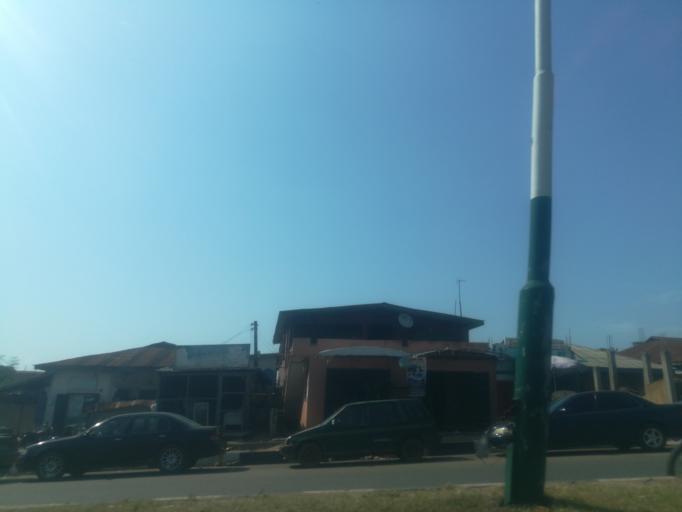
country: NG
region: Ogun
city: Abeokuta
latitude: 7.1490
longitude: 3.3433
